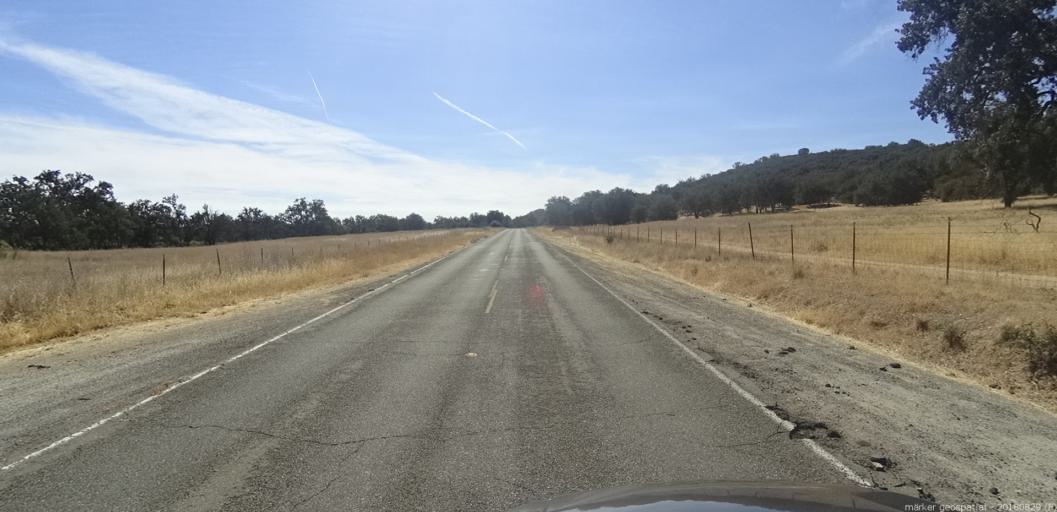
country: US
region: California
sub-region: San Luis Obispo County
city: Lake Nacimiento
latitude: 35.8965
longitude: -121.0880
